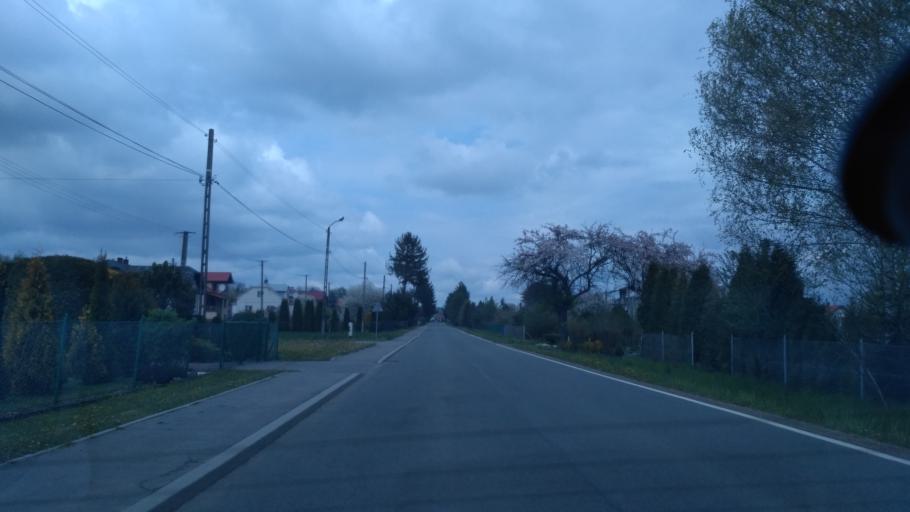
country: PL
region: Subcarpathian Voivodeship
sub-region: Powiat brzozowski
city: Jasionow
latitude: 49.6460
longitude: 21.9772
